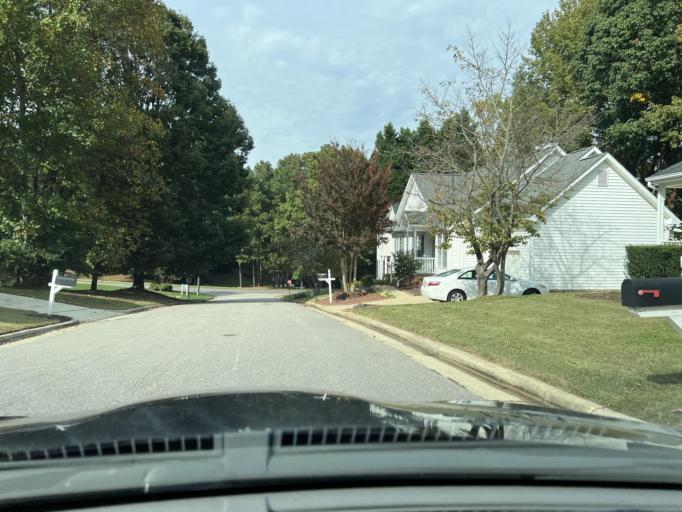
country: US
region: North Carolina
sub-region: Wake County
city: Wake Forest
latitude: 35.8975
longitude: -78.5880
